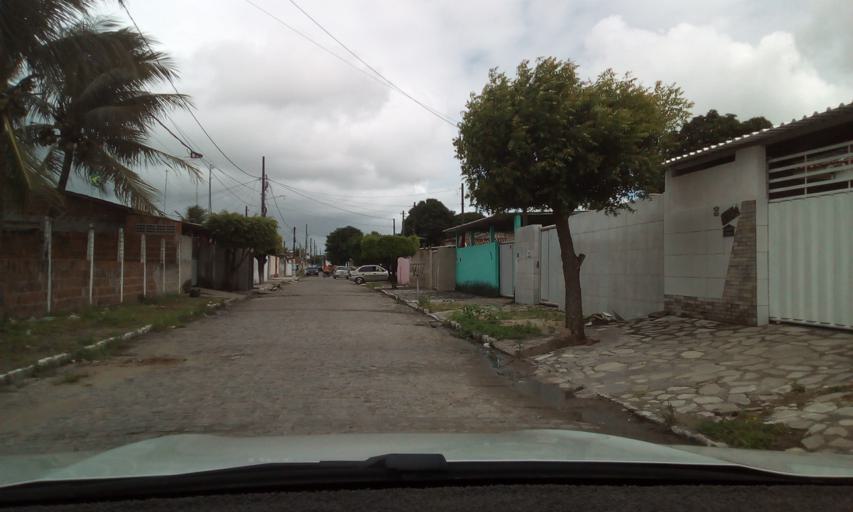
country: BR
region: Paraiba
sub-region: Santa Rita
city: Santa Rita
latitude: -7.1402
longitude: -34.9652
